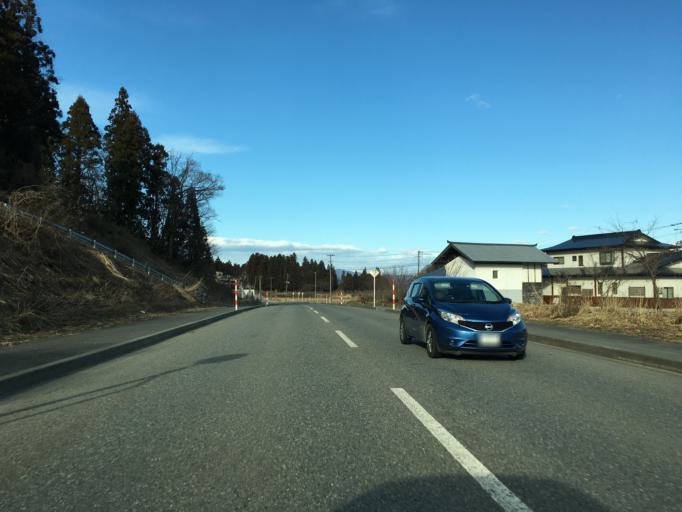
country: JP
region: Yamagata
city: Nagai
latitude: 38.0215
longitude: 139.9735
